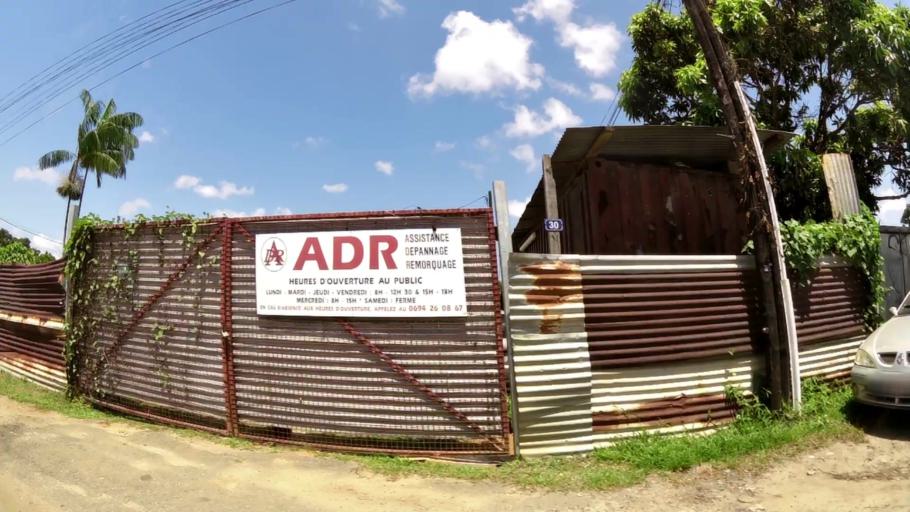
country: GF
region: Guyane
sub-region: Guyane
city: Cayenne
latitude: 4.9036
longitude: -52.3260
